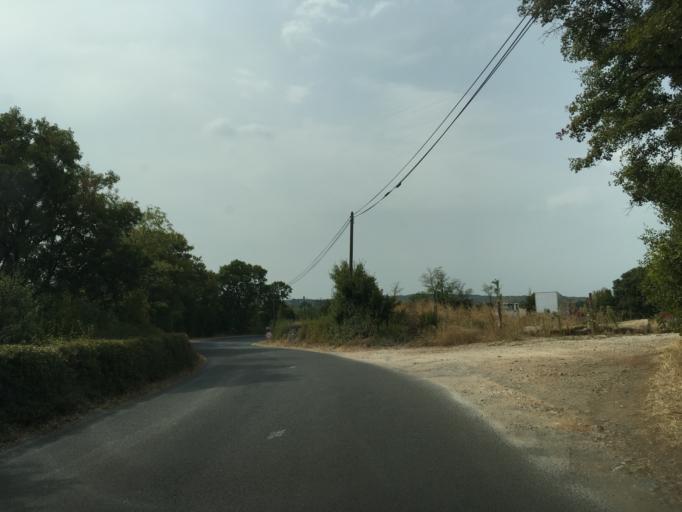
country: FR
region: Midi-Pyrenees
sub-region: Departement du Lot
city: Gramat
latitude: 44.8066
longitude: 1.6228
